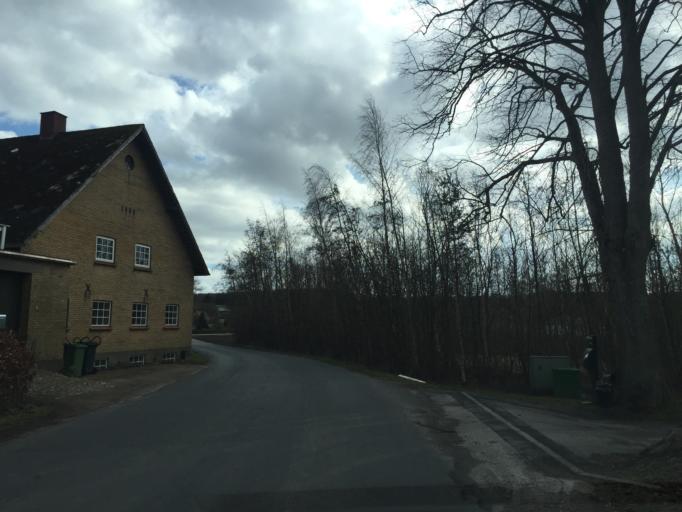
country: DK
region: South Denmark
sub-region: Svendborg Kommune
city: Svendborg
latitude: 55.1064
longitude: 10.5143
